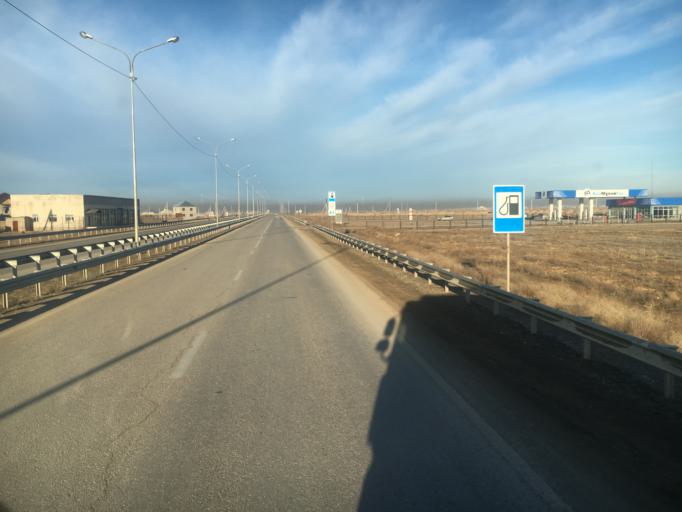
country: KZ
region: Ongtustik Qazaqstan
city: Turkestan
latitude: 43.3019
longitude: 68.3336
